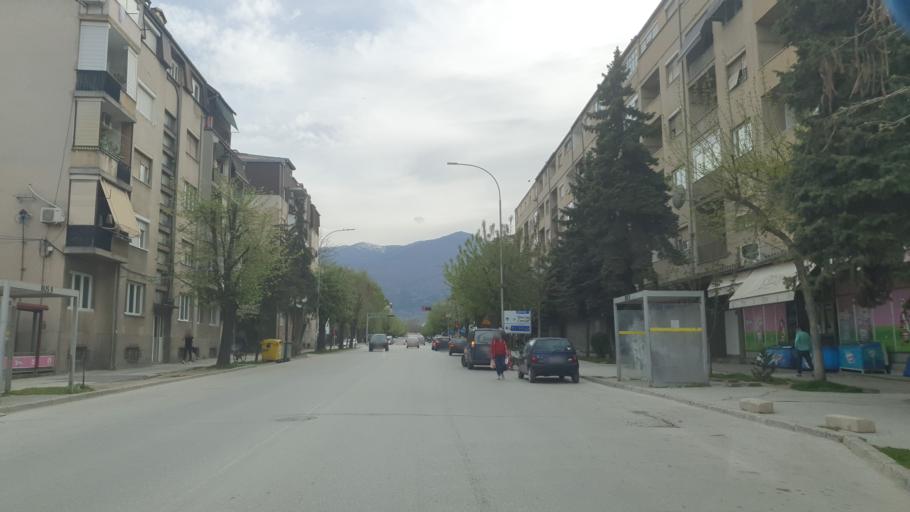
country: MK
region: Bitola
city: Bitola
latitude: 41.0358
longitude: 21.3409
